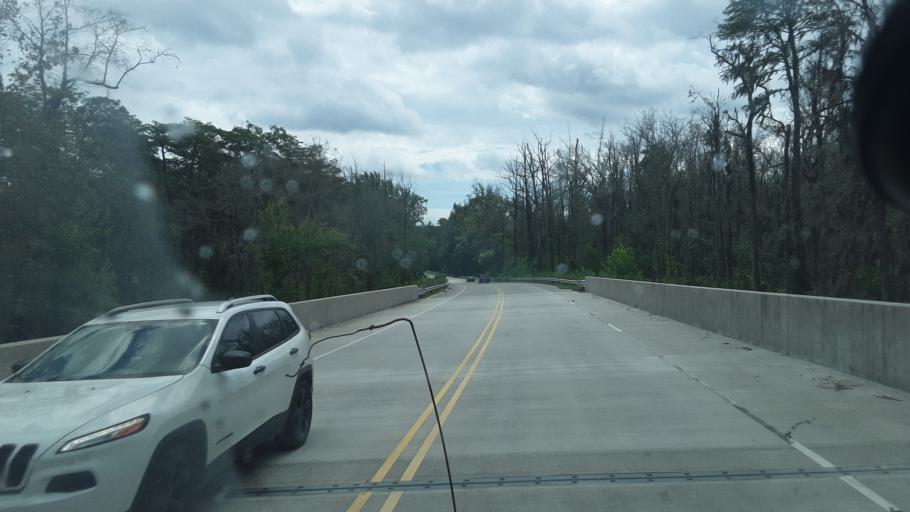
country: US
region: North Carolina
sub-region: Scotland County
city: Laurinburg
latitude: 34.6875
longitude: -79.4360
